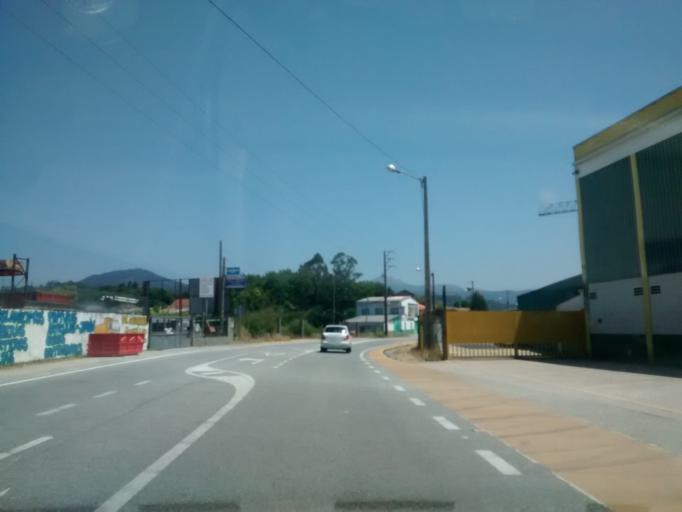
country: ES
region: Galicia
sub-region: Provincia de Pontevedra
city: Nigran
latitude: 42.1148
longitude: -8.8050
